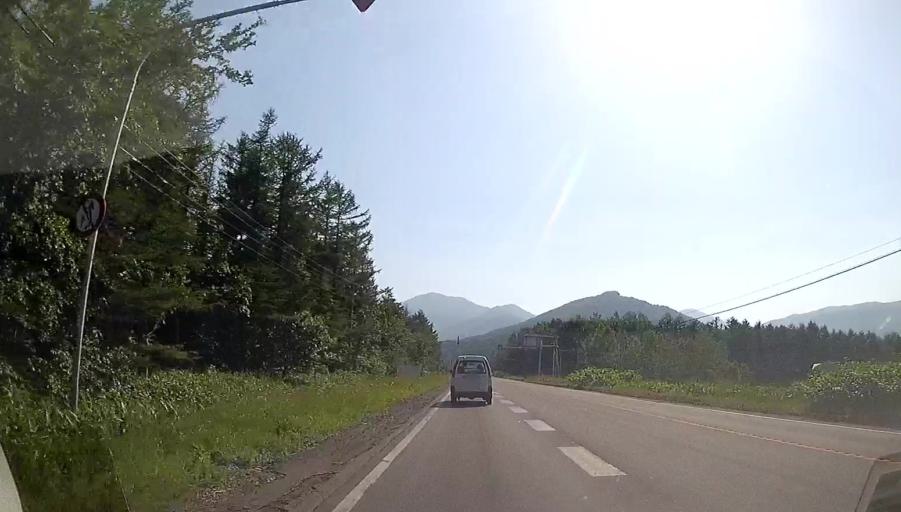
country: JP
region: Hokkaido
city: Otofuke
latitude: 42.9752
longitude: 142.8209
